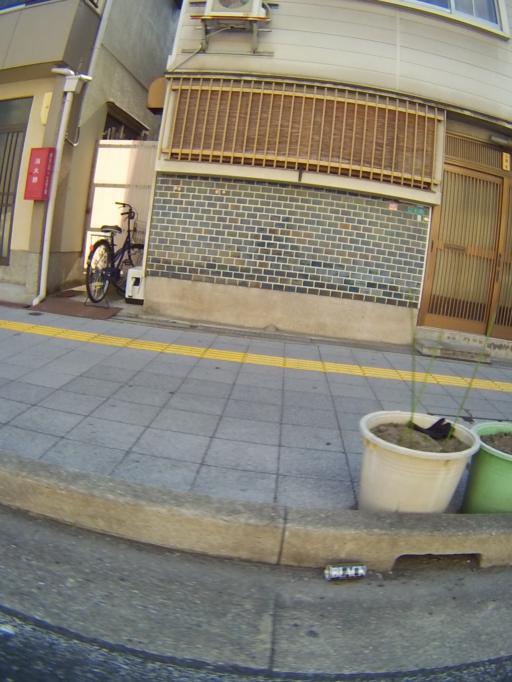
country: JP
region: Osaka
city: Osaka-shi
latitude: 34.6726
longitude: 135.4598
